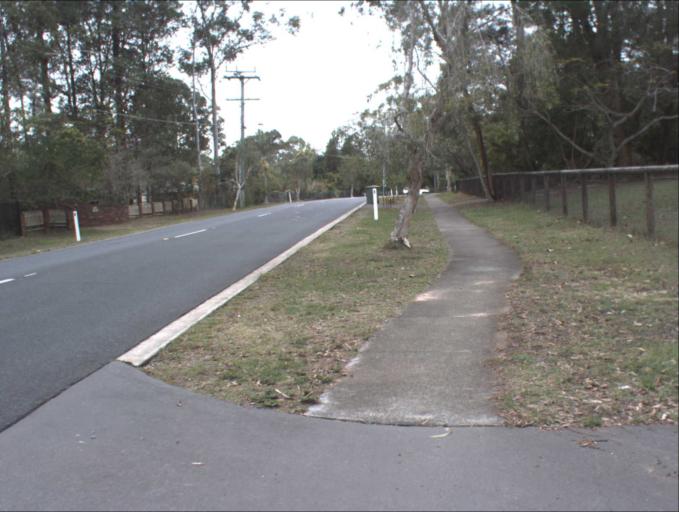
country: AU
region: Queensland
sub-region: Brisbane
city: Forest Lake
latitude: -27.6656
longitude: 153.0083
